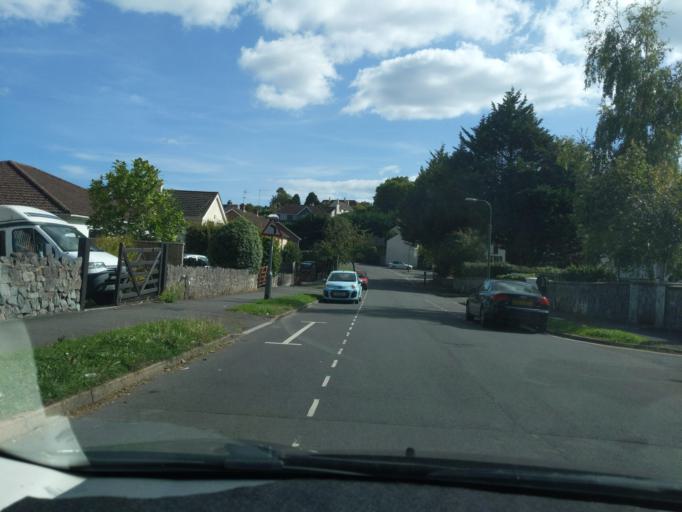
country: GB
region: England
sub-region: Devon
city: Kingskerswell
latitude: 50.4793
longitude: -3.5622
